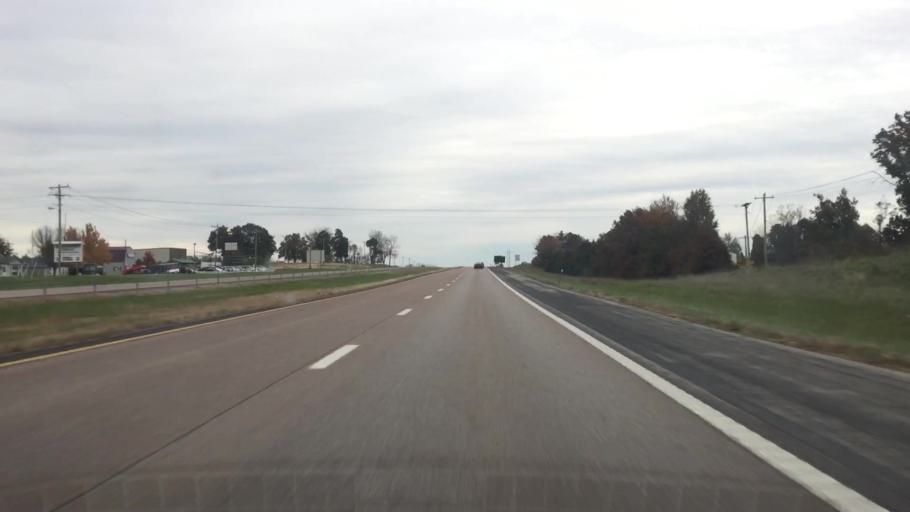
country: US
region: Missouri
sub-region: Boone County
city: Ashland
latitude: 38.7808
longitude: -92.2523
